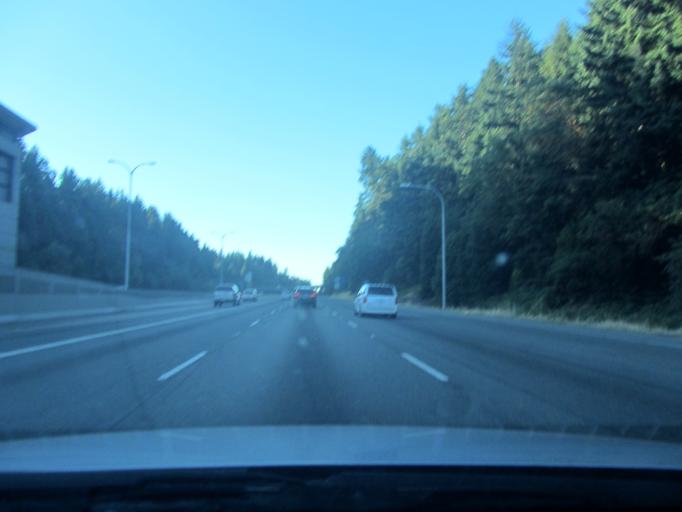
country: US
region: Washington
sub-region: Snohomish County
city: Mountlake Terrace
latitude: 47.7875
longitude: -122.3161
